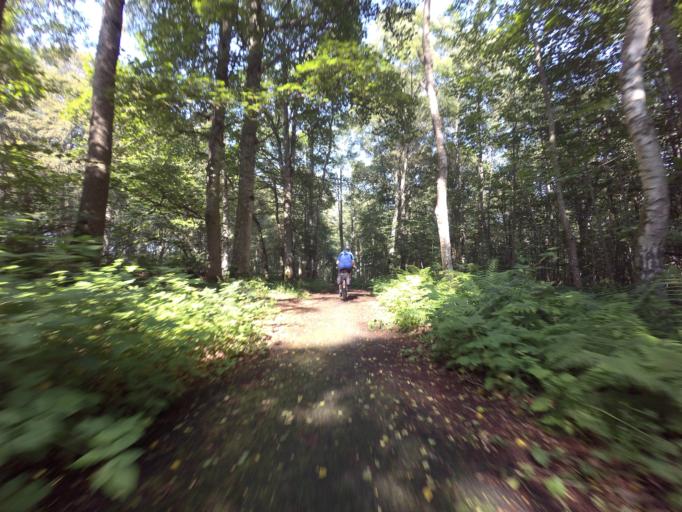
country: GB
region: Scotland
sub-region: Highland
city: Evanton
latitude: 57.6739
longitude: -4.3184
